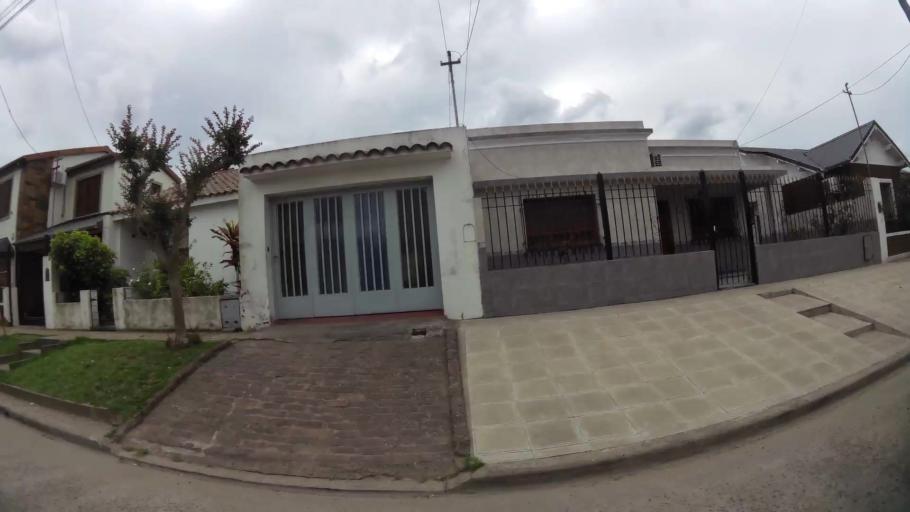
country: AR
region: Buenos Aires
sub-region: Partido de Zarate
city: Zarate
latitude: -34.1112
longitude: -59.0121
